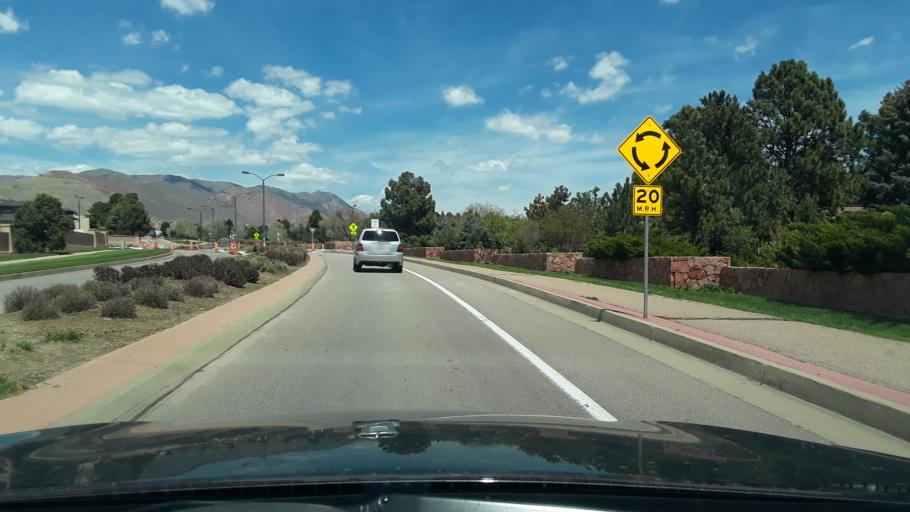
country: US
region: Colorado
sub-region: El Paso County
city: Manitou Springs
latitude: 38.8771
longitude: -104.8652
